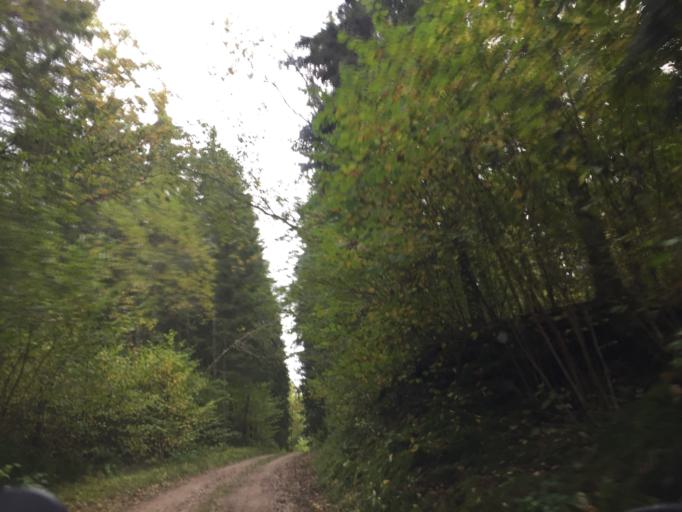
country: LV
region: Auces Novads
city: Auce
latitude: 56.5503
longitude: 23.0328
